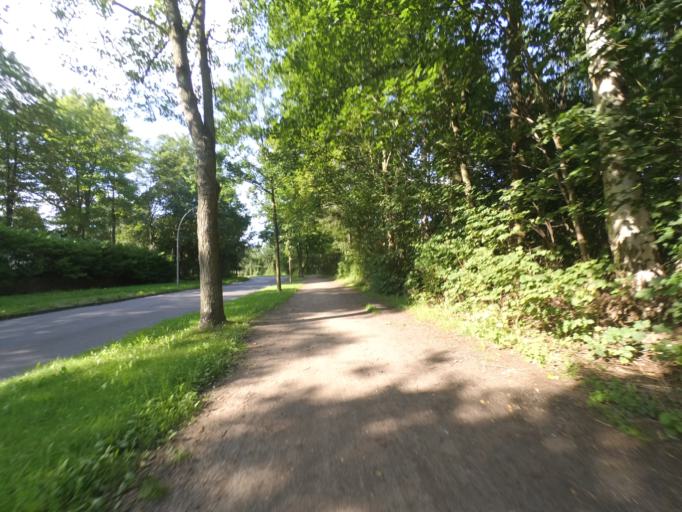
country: DE
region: Hamburg
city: Wandsbek
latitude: 53.5473
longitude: 10.1271
